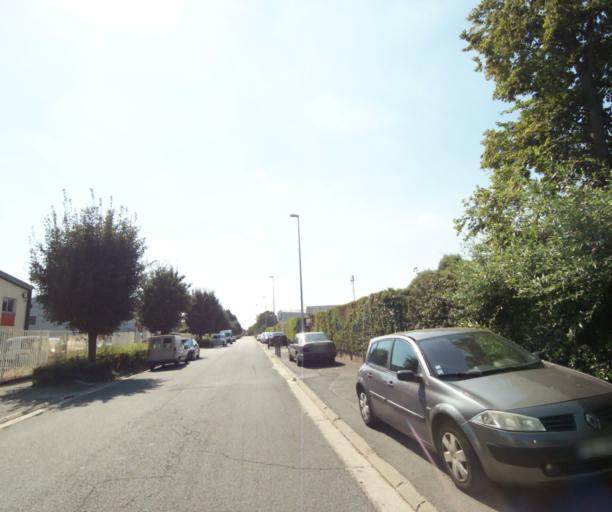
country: FR
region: Ile-de-France
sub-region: Departement de Seine-et-Marne
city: Pomponne
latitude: 48.8763
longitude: 2.6871
